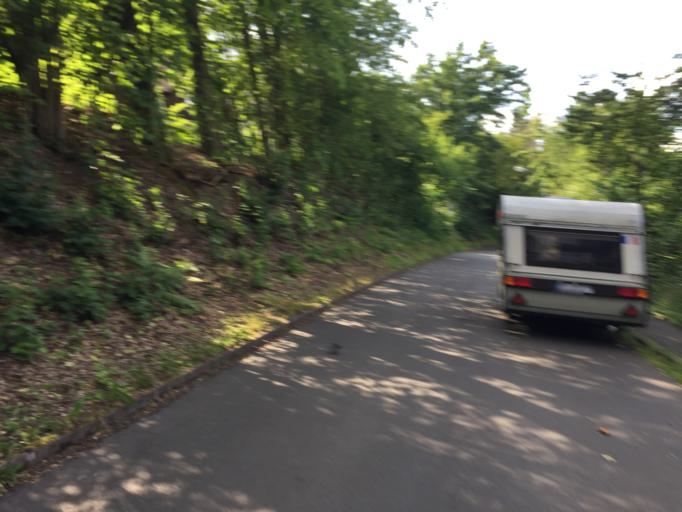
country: DE
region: Hesse
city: Schwalmstadt
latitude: 50.9155
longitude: 9.1739
